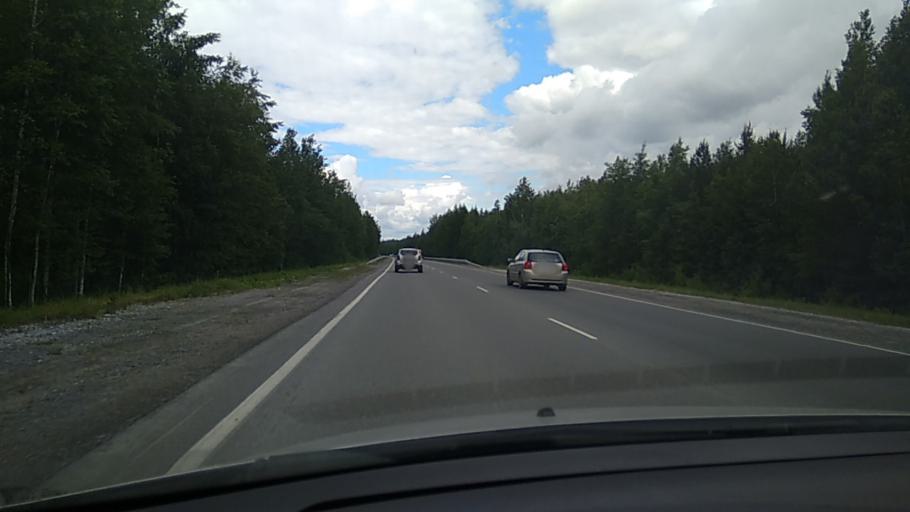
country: RU
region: Sverdlovsk
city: Neyvo-Rudyanka
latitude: 57.3472
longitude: 60.2668
